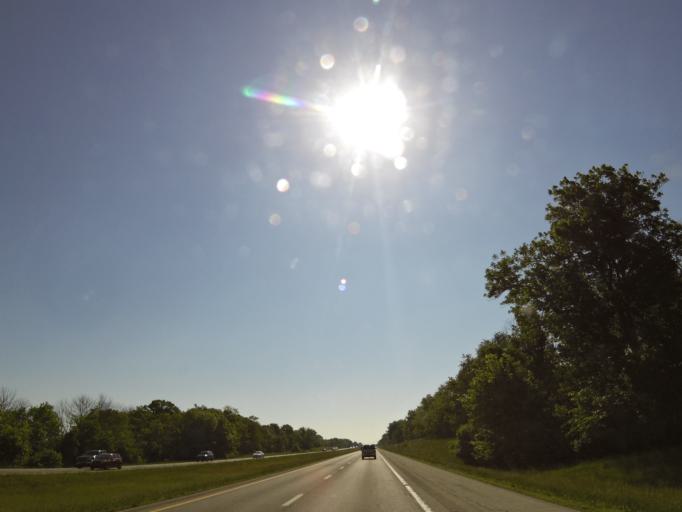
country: US
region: Kentucky
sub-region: Shelby County
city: Shelbyville
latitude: 38.1849
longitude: -85.2286
